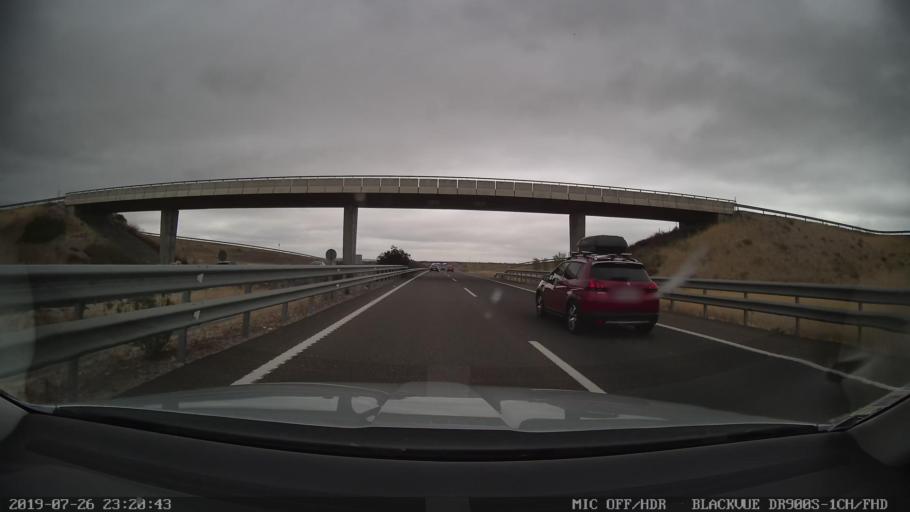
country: ES
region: Extremadura
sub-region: Provincia de Caceres
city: Miajadas
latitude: 39.1221
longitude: -5.9646
